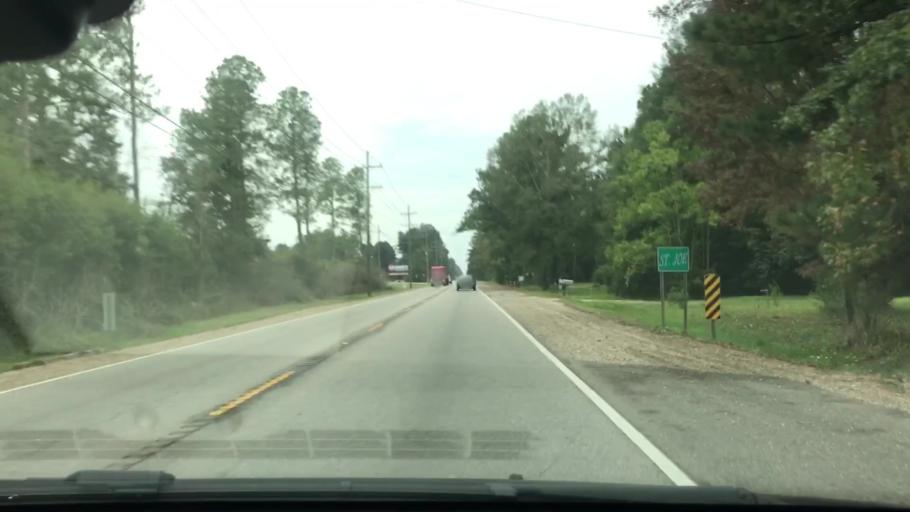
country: US
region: Louisiana
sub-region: Saint Tammany Parish
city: Pearl River
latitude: 30.3519
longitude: -89.7541
